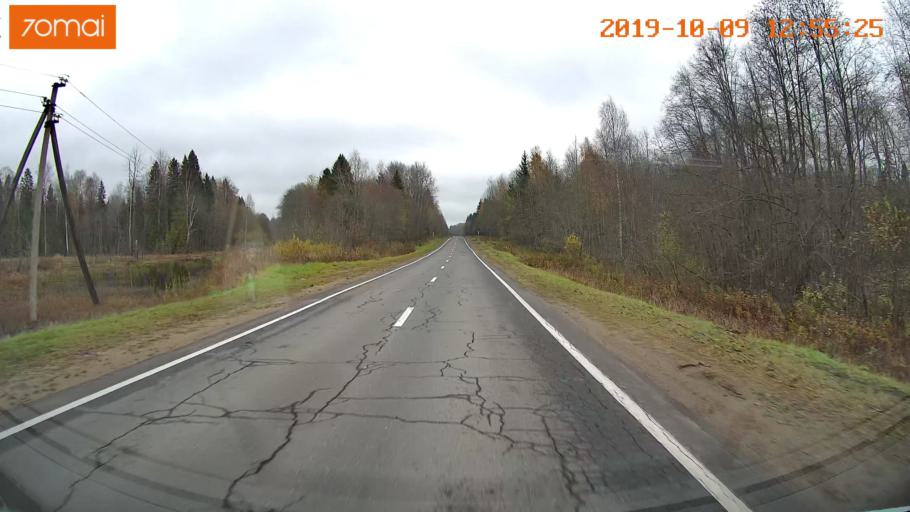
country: RU
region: Jaroslavl
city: Prechistoye
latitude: 58.4000
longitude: 40.3929
